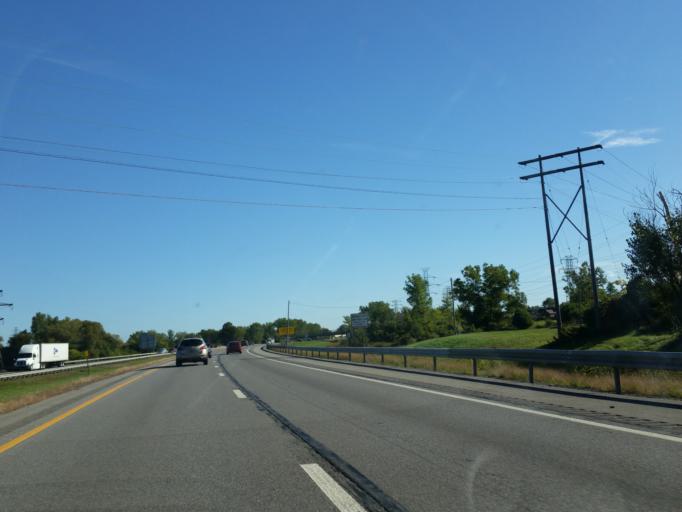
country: US
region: New York
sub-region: Erie County
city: Blasdell
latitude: 42.8045
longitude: -78.8121
